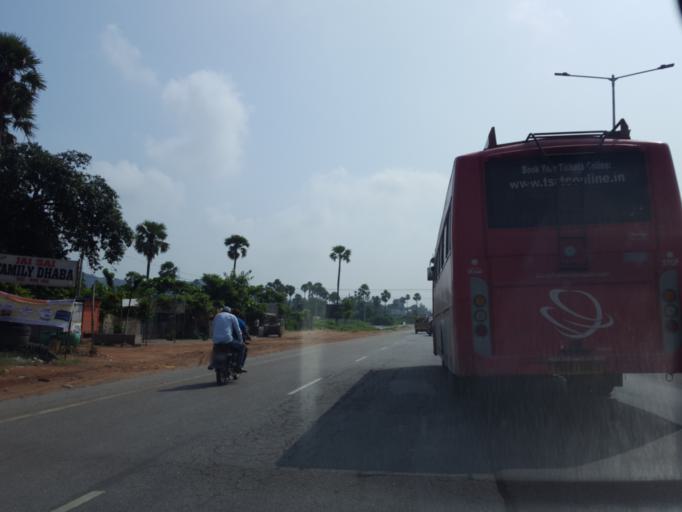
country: IN
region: Telangana
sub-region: Rangareddi
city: Ghatkesar
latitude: 17.3069
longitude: 78.7103
